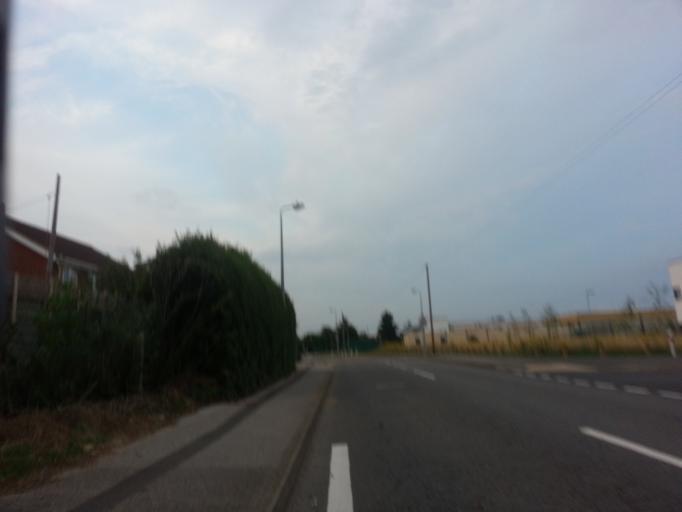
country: GB
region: England
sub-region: Suffolk
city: Ipswich
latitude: 52.0306
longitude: 1.1860
